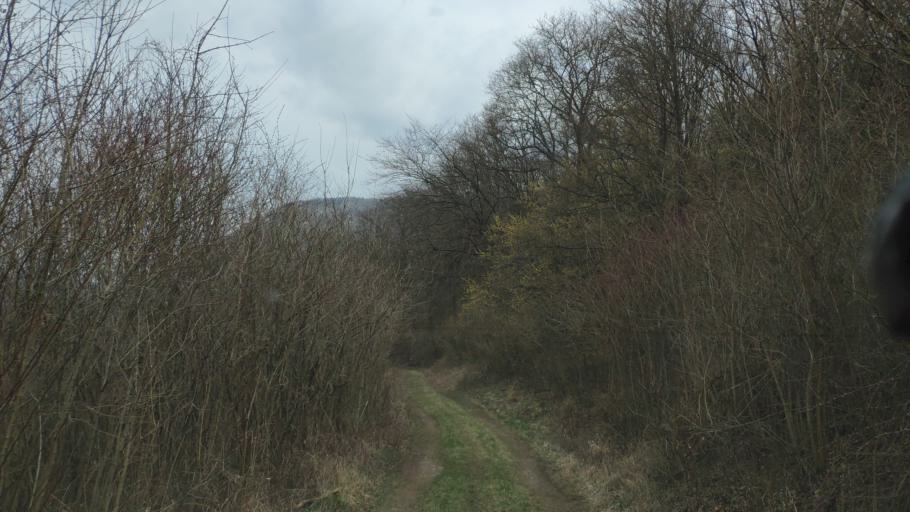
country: SK
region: Kosicky
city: Roznava
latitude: 48.6235
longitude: 20.3887
